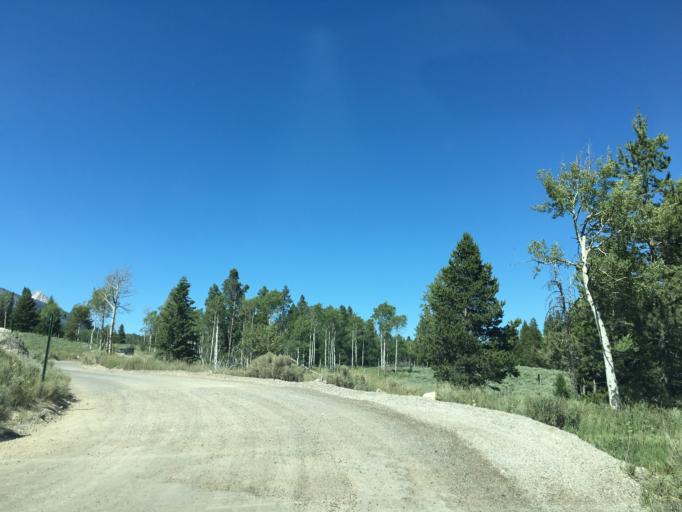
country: US
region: Wyoming
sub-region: Teton County
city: Moose Wilson Road
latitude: 43.6083
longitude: -110.7925
